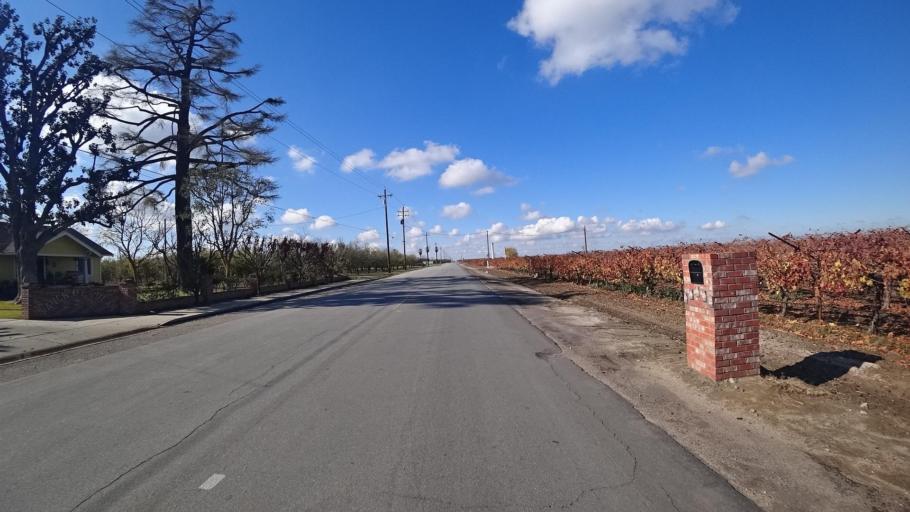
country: US
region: California
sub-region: Kern County
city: McFarland
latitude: 35.6744
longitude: -119.2458
